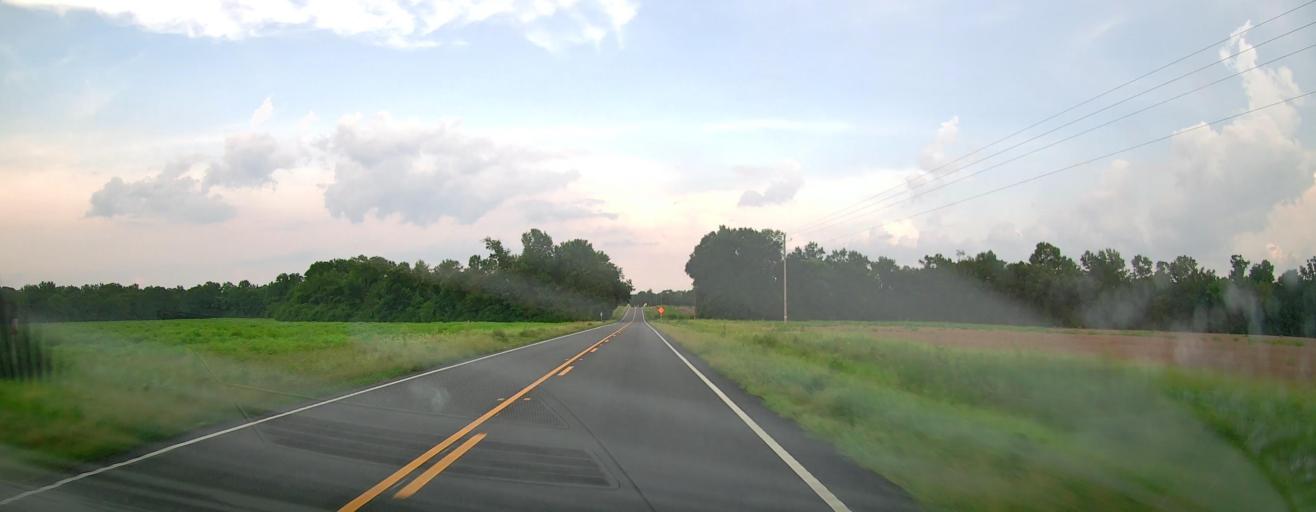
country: US
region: Georgia
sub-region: Dodge County
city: Chester
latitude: 32.5488
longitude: -83.1255
